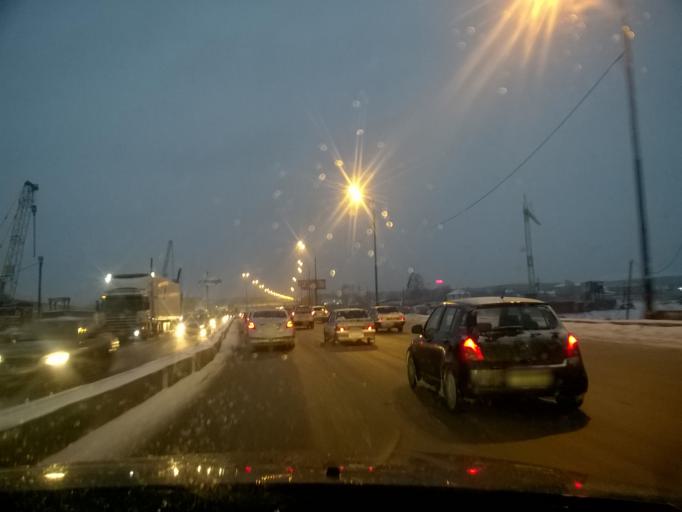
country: RU
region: Moscow
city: Solntsevo
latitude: 55.6155
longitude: 37.3793
